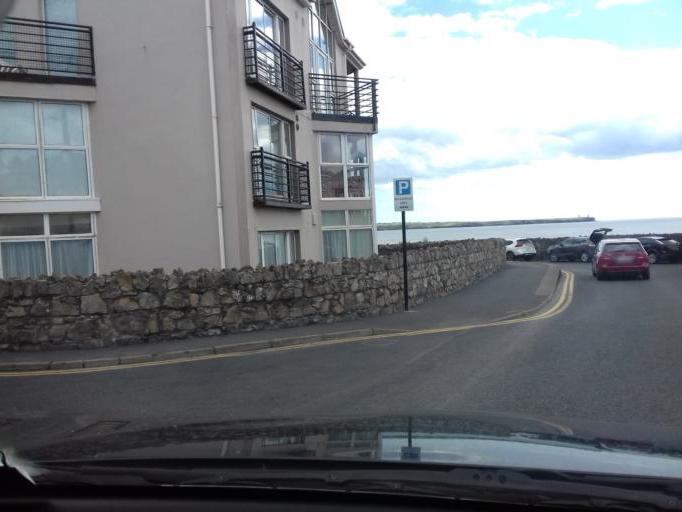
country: IE
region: Munster
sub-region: Waterford
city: Tra Mhor
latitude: 52.1595
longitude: -7.1501
